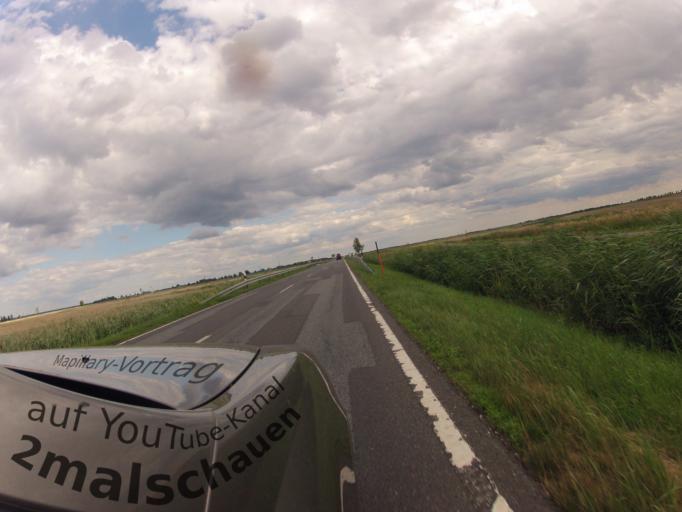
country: DE
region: Mecklenburg-Vorpommern
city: Lassan
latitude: 53.8728
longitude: 13.8087
